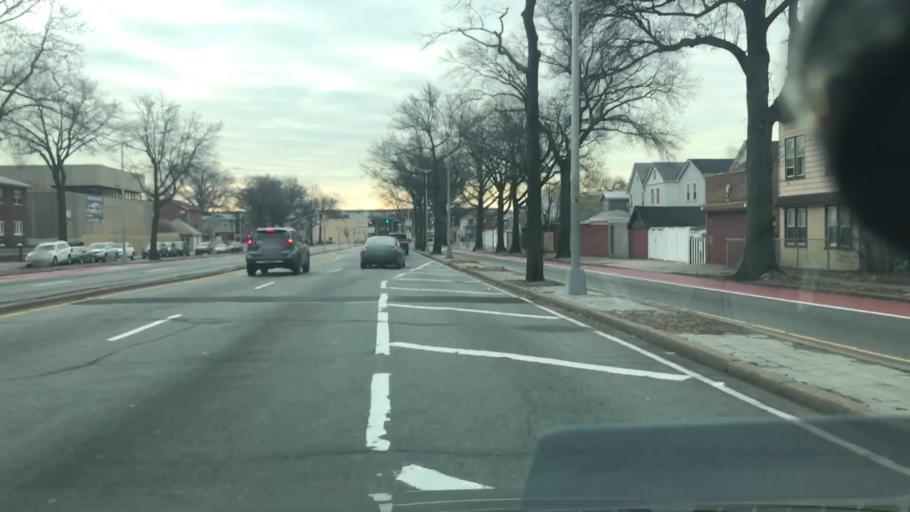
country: US
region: New York
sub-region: Queens County
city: Borough of Queens
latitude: 40.6837
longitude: -73.8459
